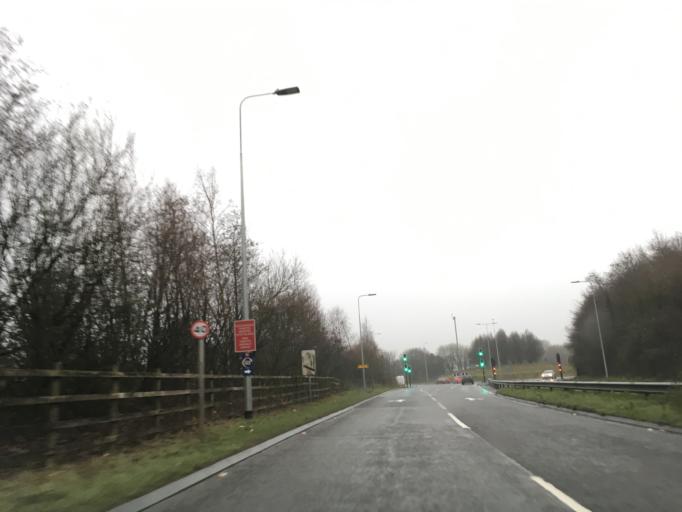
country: GB
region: Wales
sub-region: Newport
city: Marshfield
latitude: 51.5352
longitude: -3.1268
